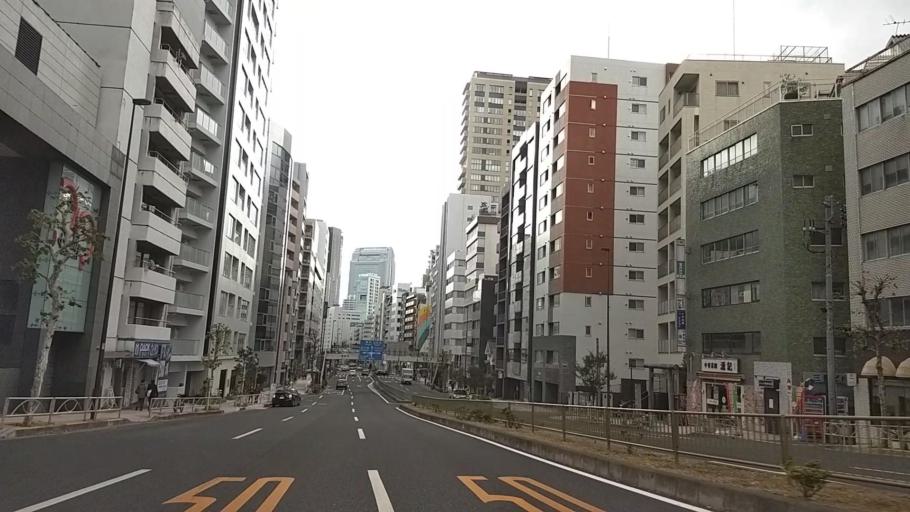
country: JP
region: Tokyo
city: Tokyo
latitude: 35.6589
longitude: 139.7433
